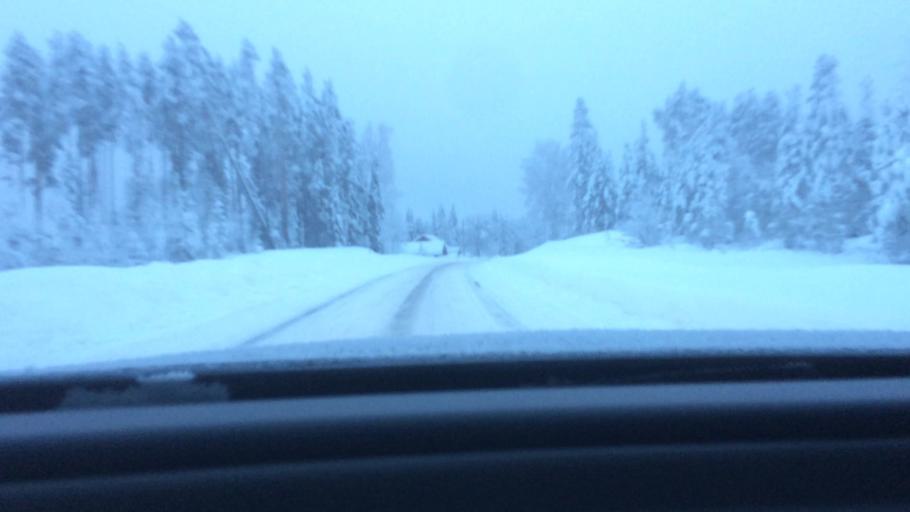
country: SE
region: Gaevleborg
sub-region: Ljusdals Kommun
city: Farila
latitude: 61.7744
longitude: 15.1719
